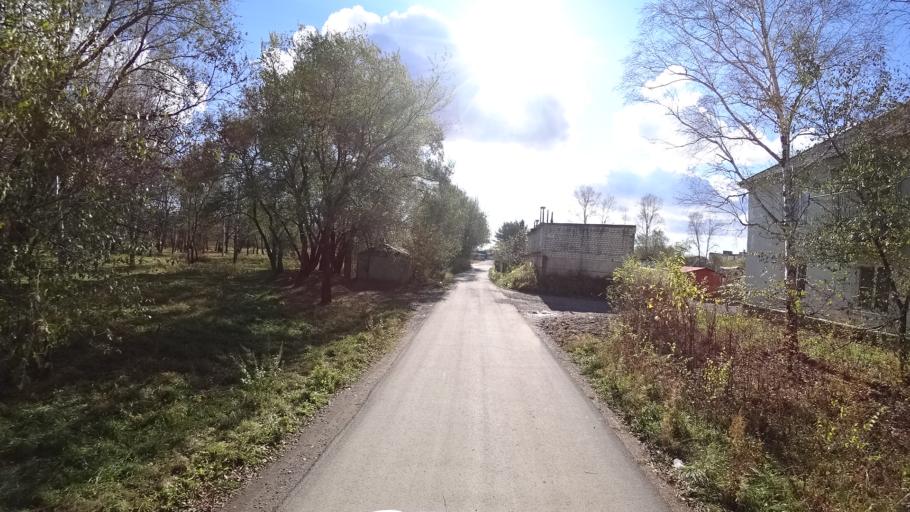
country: RU
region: Khabarovsk Krai
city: Amursk
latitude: 50.0998
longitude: 136.5034
